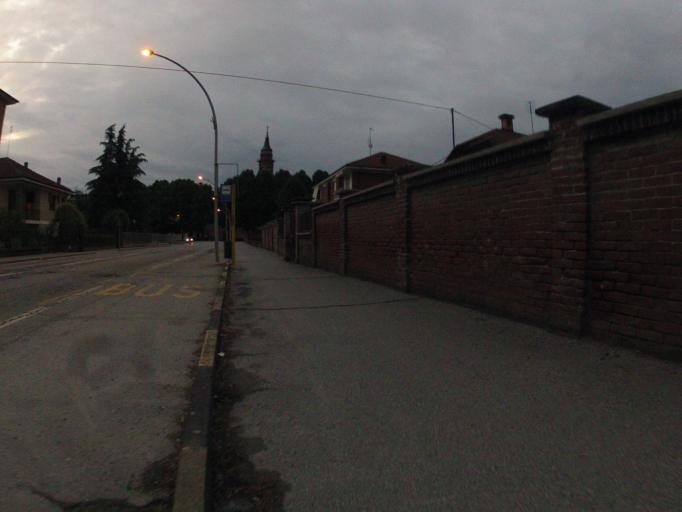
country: IT
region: Piedmont
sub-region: Provincia di Cuneo
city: Moretta
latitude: 44.7660
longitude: 7.5309
